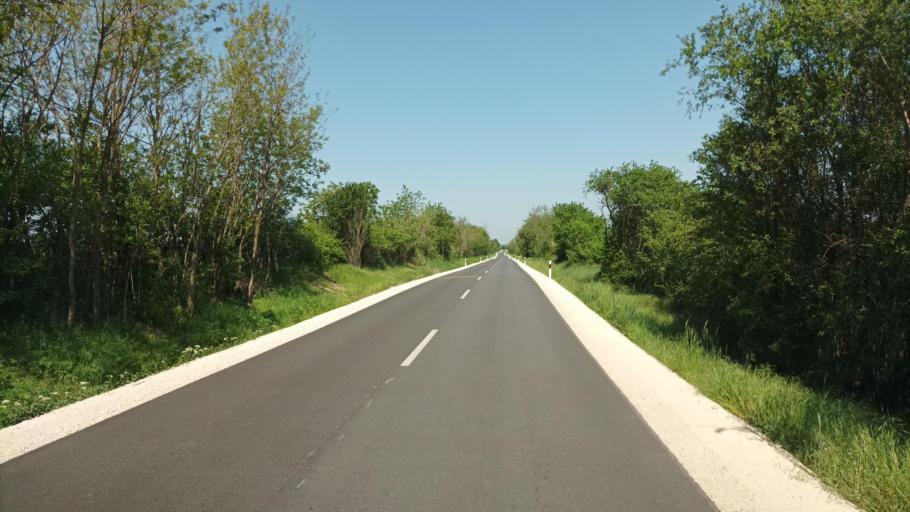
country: HU
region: Pest
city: Gomba
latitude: 47.3772
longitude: 19.5169
